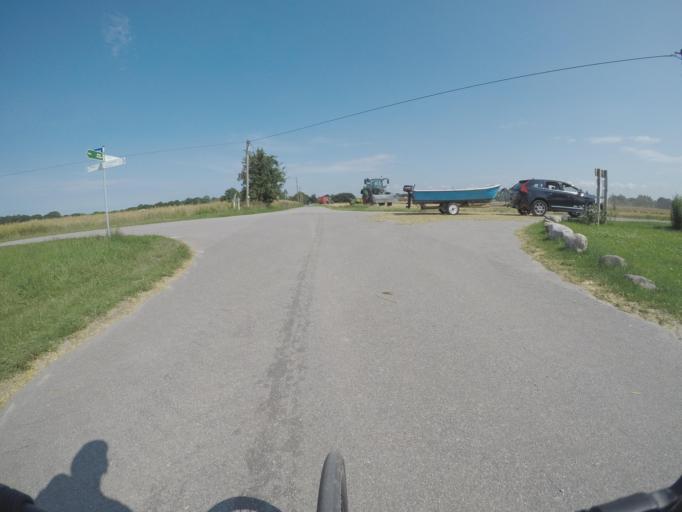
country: DE
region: Mecklenburg-Vorpommern
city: Gingst
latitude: 54.4375
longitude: 13.1757
